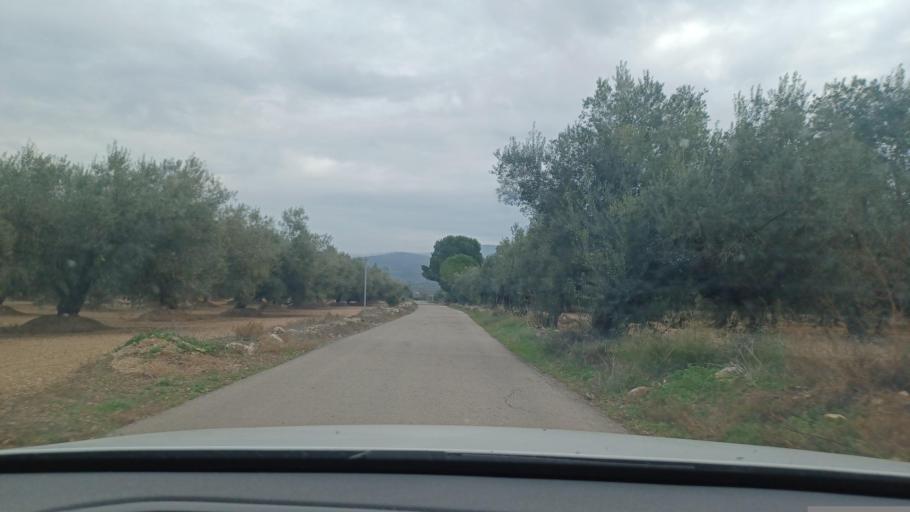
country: ES
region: Catalonia
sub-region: Provincia de Tarragona
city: Santa Barbara
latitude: 40.6669
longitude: 0.4446
